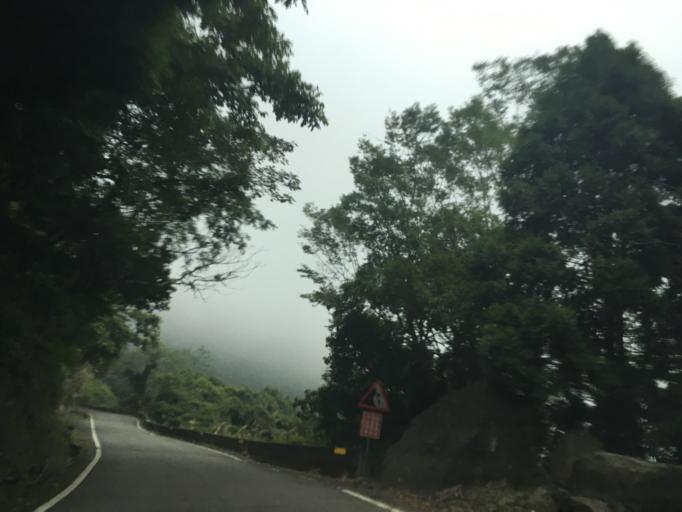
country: TW
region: Taiwan
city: Fengyuan
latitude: 24.2452
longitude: 120.9235
